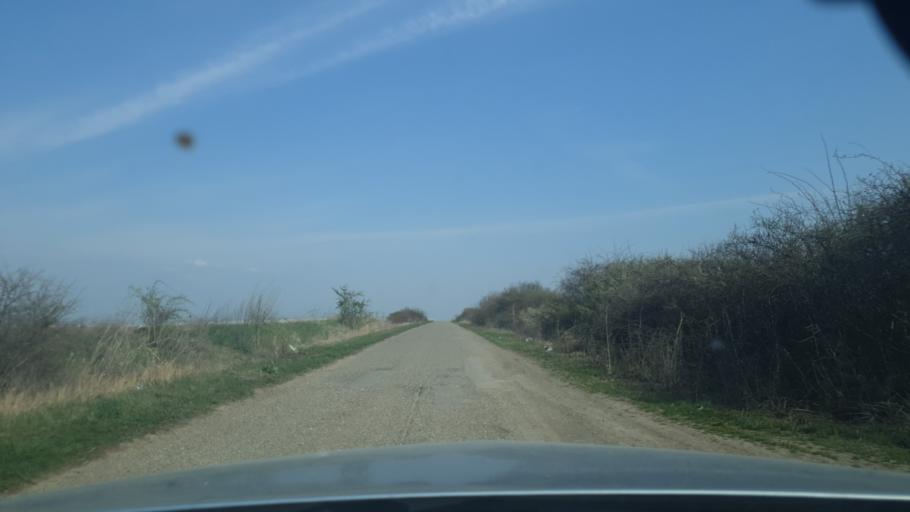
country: RS
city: Putinci
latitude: 45.0442
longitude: 19.9455
